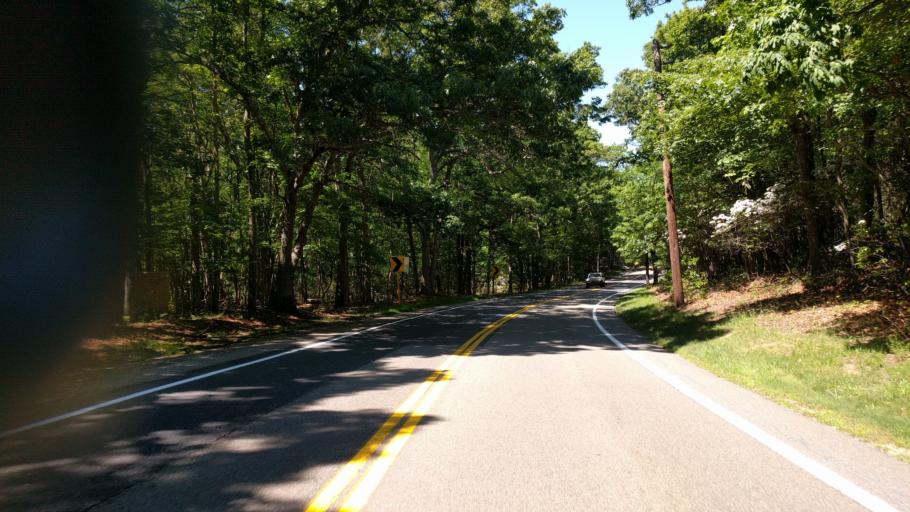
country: US
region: New York
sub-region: Suffolk County
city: Noyack
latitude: 40.9744
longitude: -72.3768
